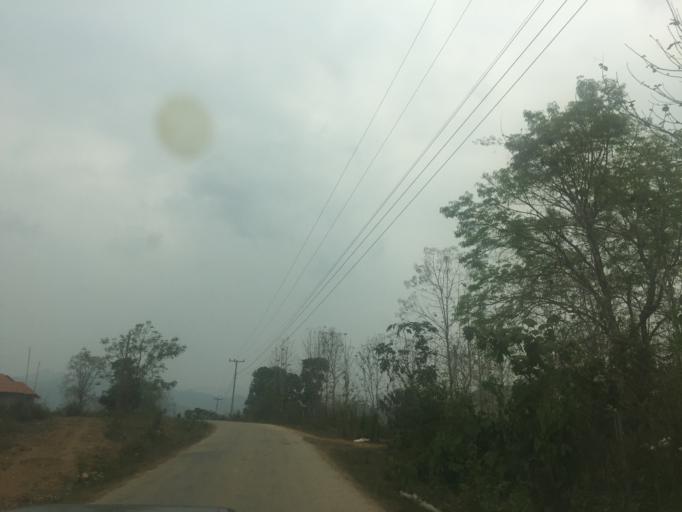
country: LA
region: Vientiane
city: Muang Sanakham
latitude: 18.3824
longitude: 101.5413
